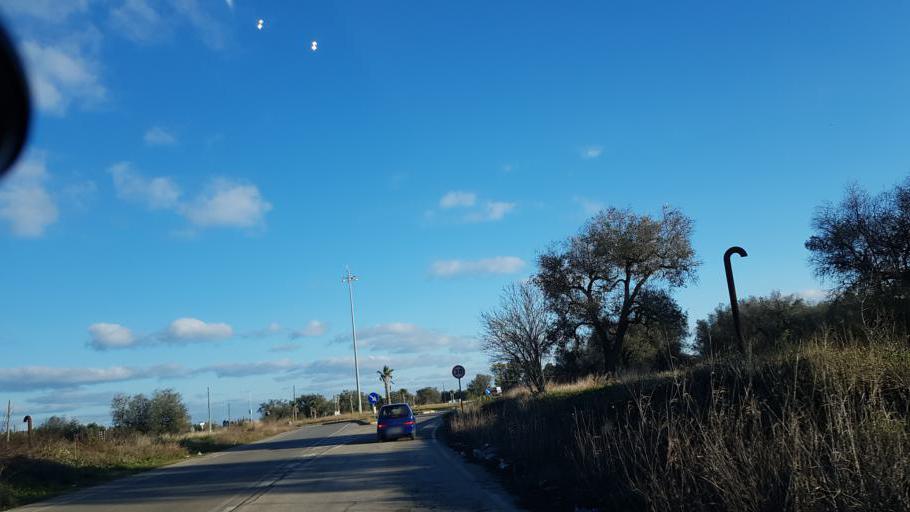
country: IT
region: Apulia
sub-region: Provincia di Brindisi
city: San Pietro Vernotico
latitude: 40.4771
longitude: 18.0063
